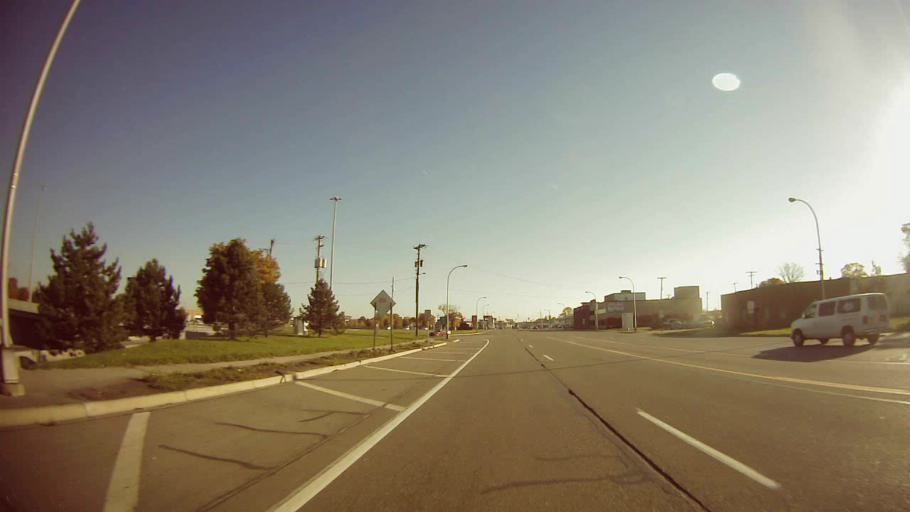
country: US
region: Michigan
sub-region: Wayne County
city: Dearborn
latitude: 42.3270
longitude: -83.1592
